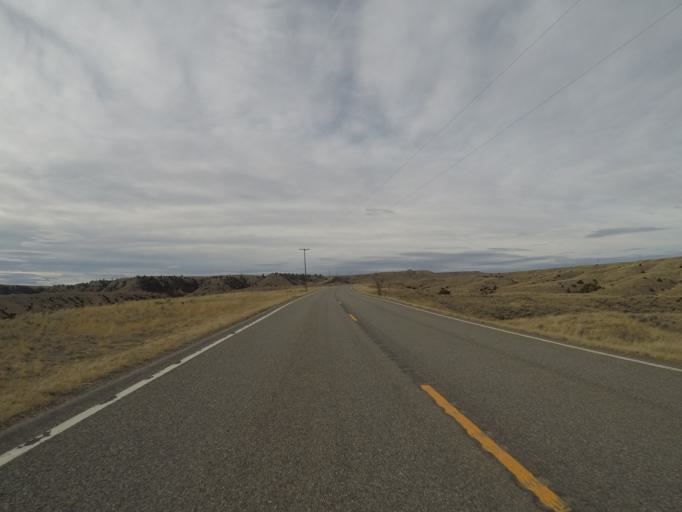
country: US
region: Montana
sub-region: Yellowstone County
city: Laurel
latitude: 45.8497
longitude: -108.7456
